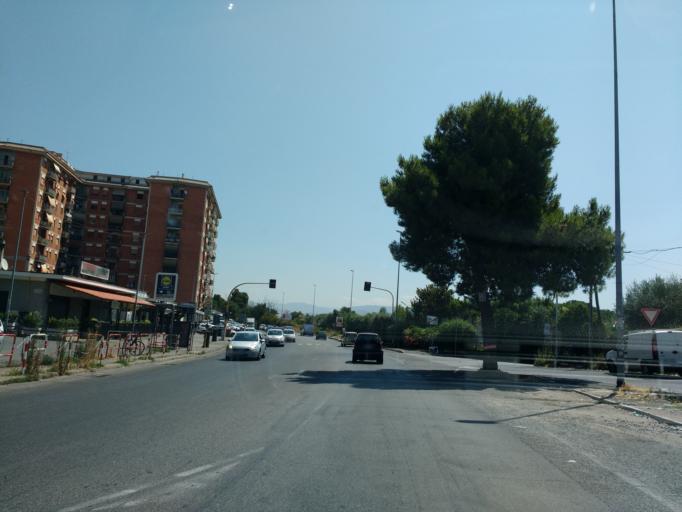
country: IT
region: Latium
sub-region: Citta metropolitana di Roma Capitale
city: Setteville
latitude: 41.9413
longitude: 12.6487
